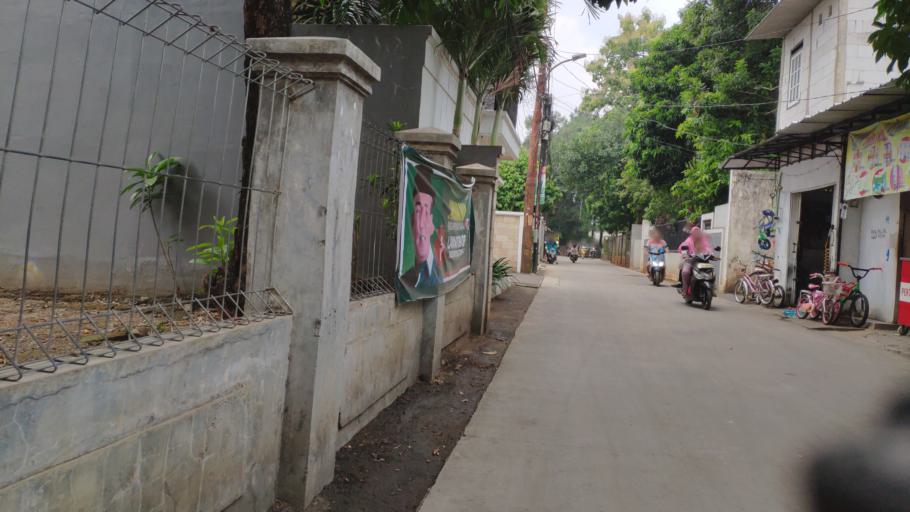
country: ID
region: West Java
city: Depok
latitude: -6.3126
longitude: 106.8309
